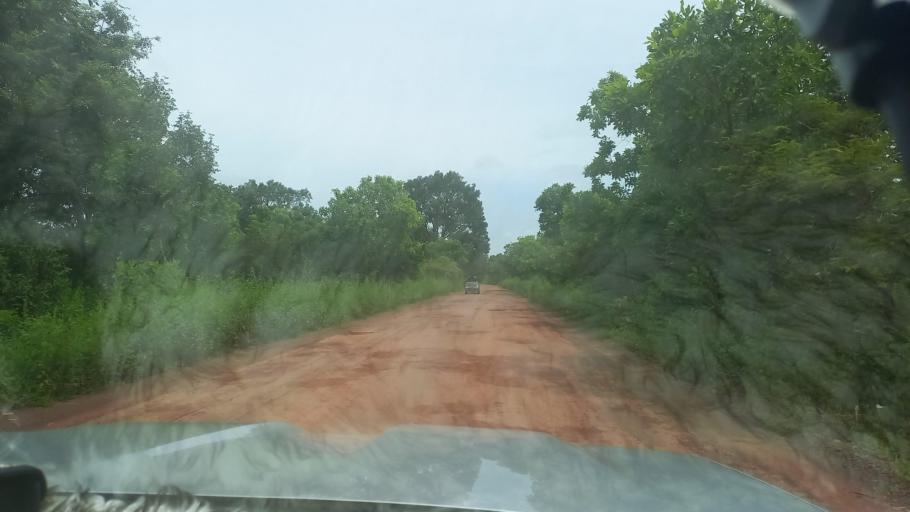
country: SN
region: Kolda
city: Marsassoum
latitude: 12.9042
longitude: -16.0199
